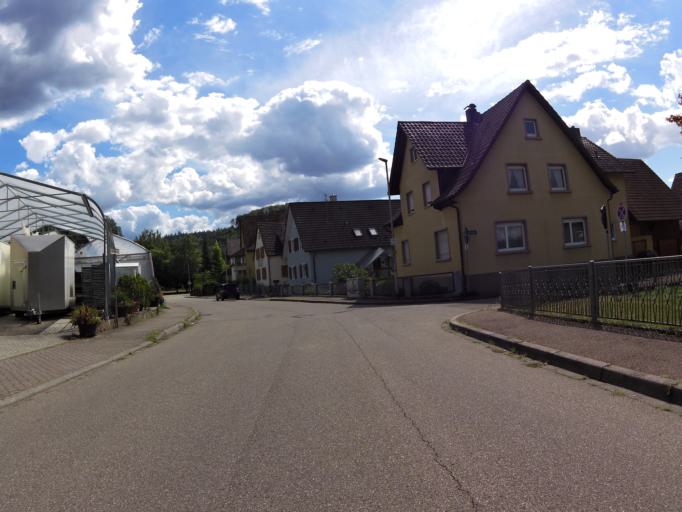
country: DE
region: Baden-Wuerttemberg
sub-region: Freiburg Region
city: Lahr
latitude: 48.3121
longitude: 7.8631
